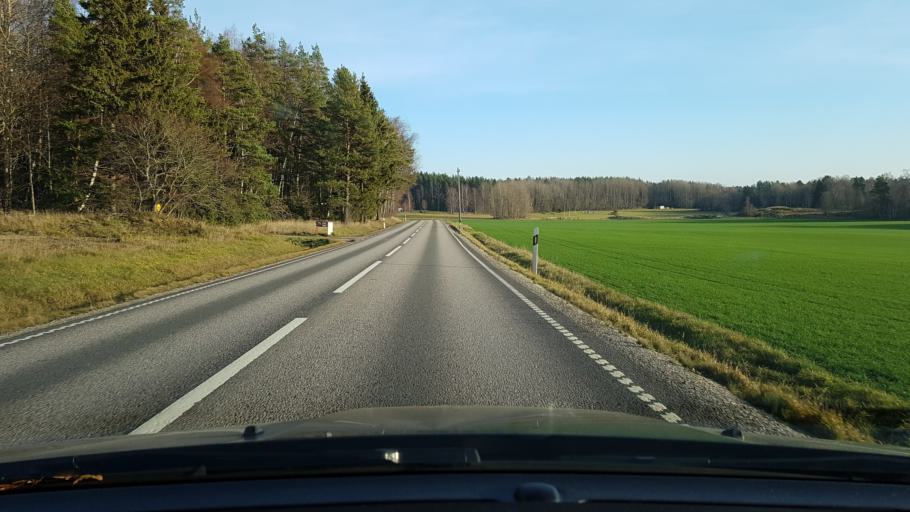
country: SE
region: Stockholm
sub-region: Norrtalje Kommun
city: Nykvarn
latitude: 59.7403
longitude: 18.1941
